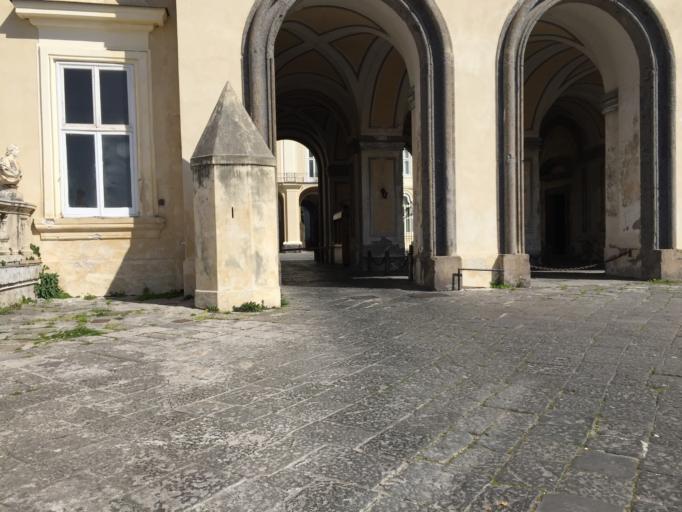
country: IT
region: Campania
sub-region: Provincia di Napoli
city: Portici
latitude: 40.8111
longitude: 14.3425
